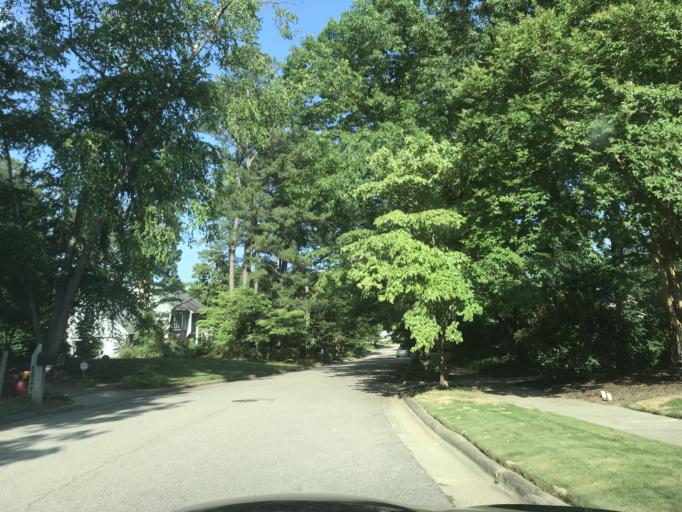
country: US
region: North Carolina
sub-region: Wake County
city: West Raleigh
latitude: 35.8734
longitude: -78.6115
